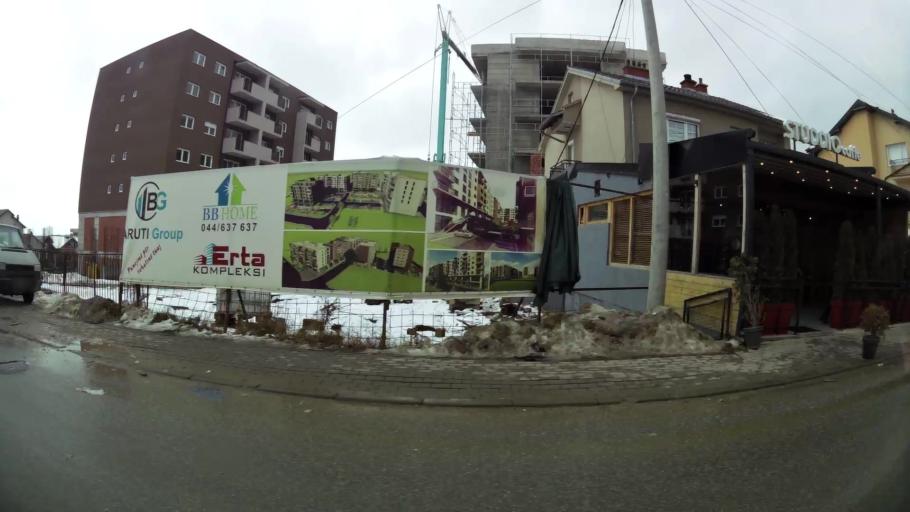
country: XK
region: Pristina
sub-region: Komuna e Prishtines
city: Pristina
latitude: 42.6543
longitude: 21.1905
